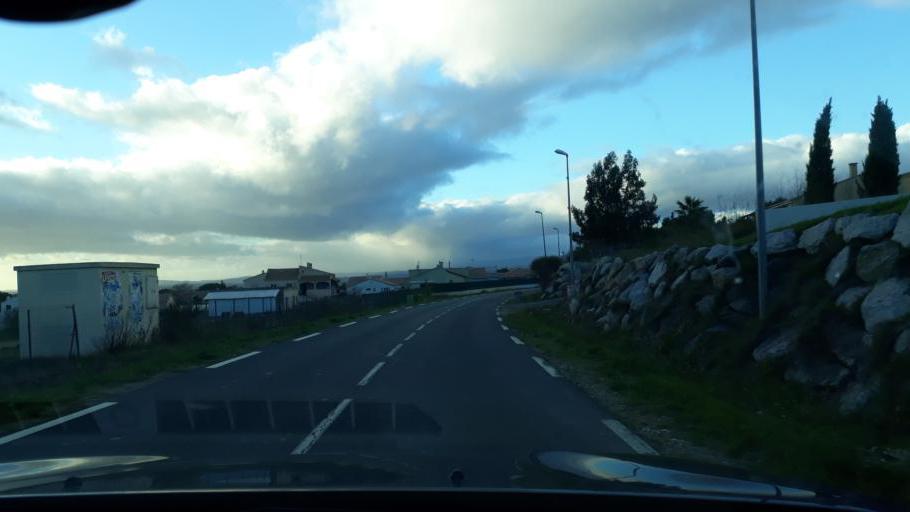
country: FR
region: Languedoc-Roussillon
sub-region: Departement de l'Herault
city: Nissan-lez-Enserune
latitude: 43.2853
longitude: 3.1392
